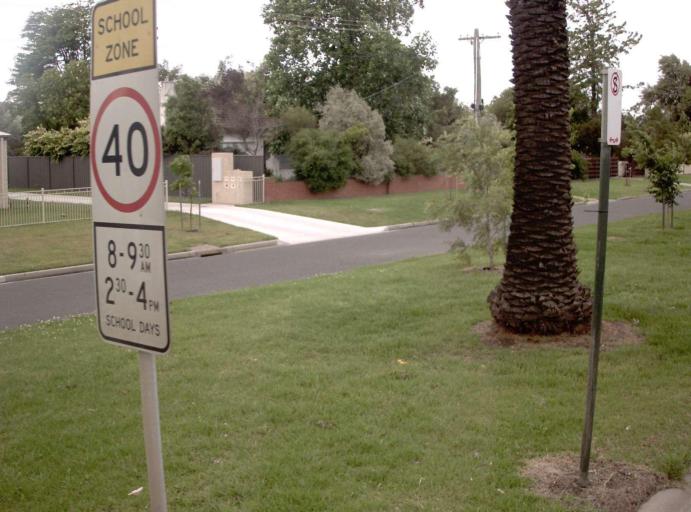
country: AU
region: Victoria
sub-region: Wellington
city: Sale
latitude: -38.0951
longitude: 147.0686
